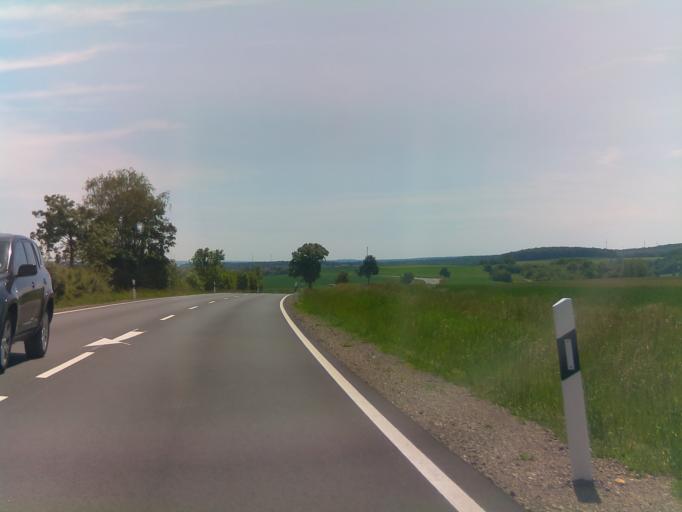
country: DE
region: Bavaria
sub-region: Regierungsbezirk Unterfranken
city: Poppenhausen
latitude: 50.1255
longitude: 10.1491
